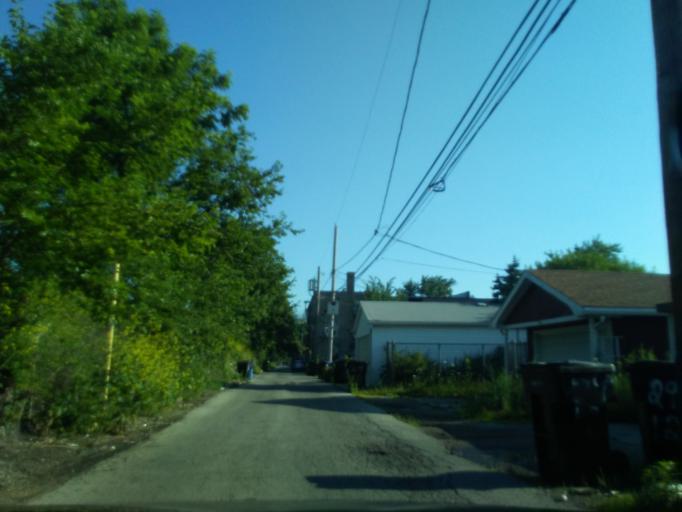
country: US
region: Illinois
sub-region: Cook County
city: Oak Park
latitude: 41.9338
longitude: -87.7417
